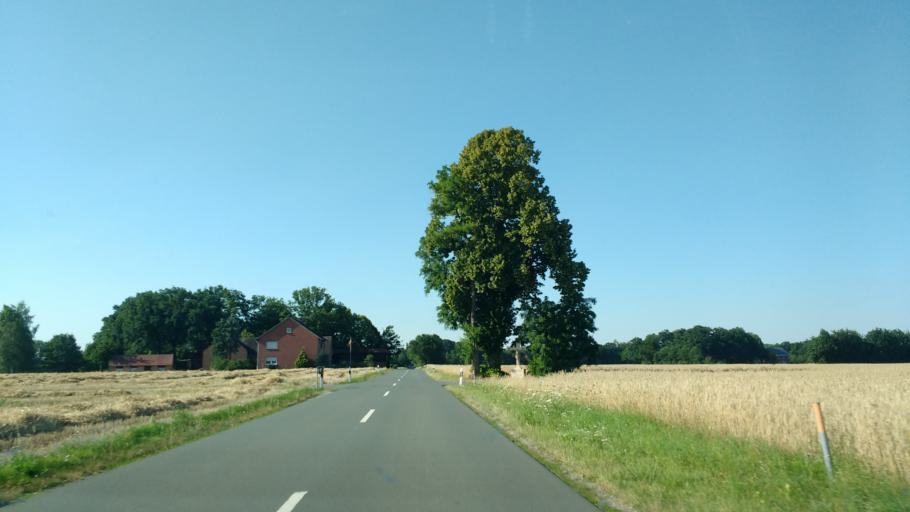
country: DE
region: North Rhine-Westphalia
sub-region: Regierungsbezirk Detmold
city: Delbruck
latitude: 51.7226
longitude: 8.4928
